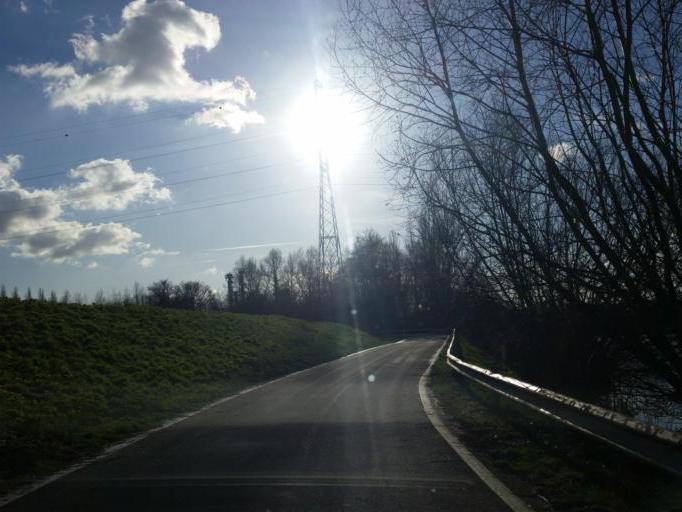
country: BE
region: Flanders
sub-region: Provincie Antwerpen
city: Zwijndrecht
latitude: 51.2948
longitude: 4.2880
